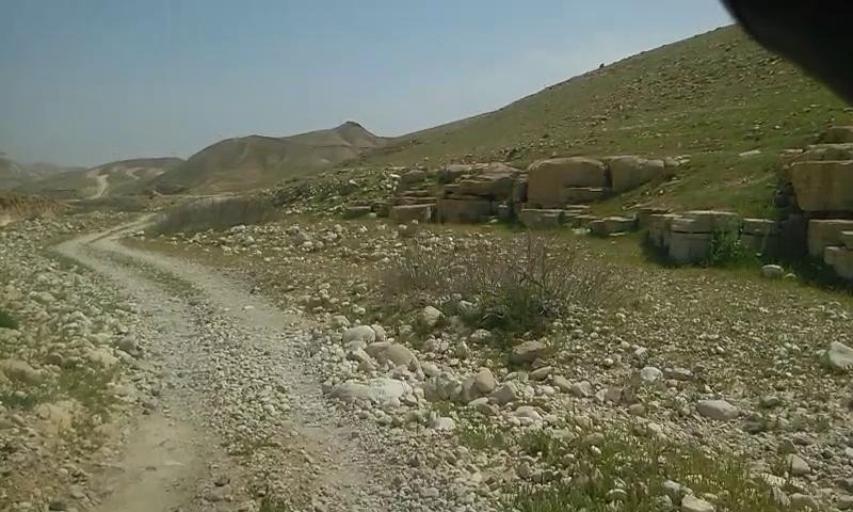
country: PS
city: `Arab ar Rashaydah
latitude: 31.5075
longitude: 35.2842
